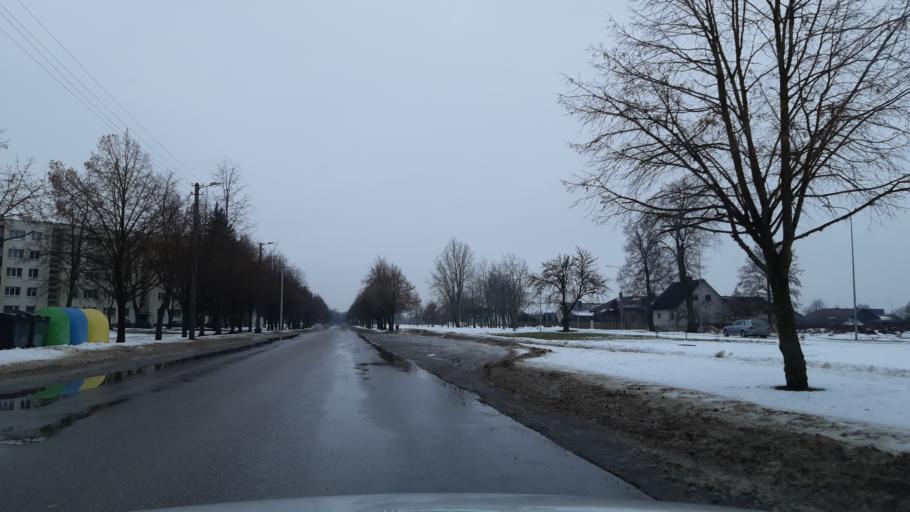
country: LT
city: Vilkaviskis
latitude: 54.6575
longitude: 23.0298
